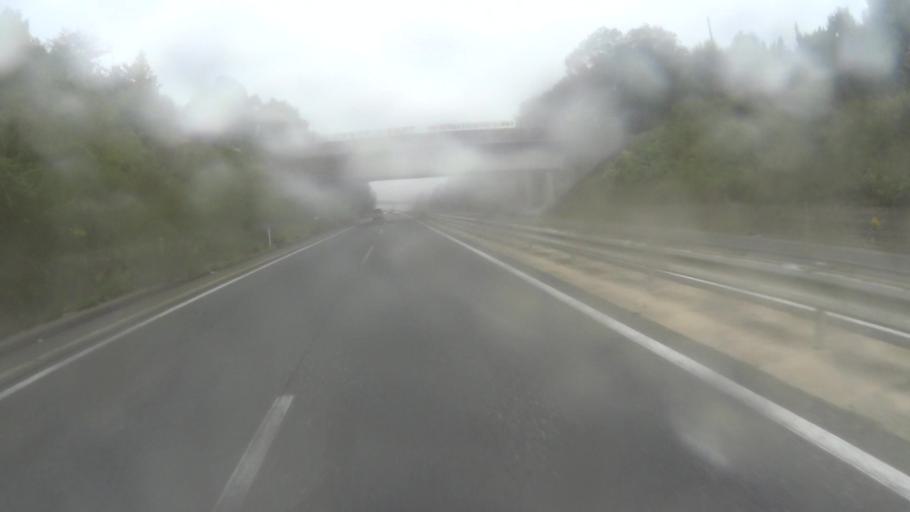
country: JP
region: Kyoto
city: Kameoka
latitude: 34.9913
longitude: 135.5869
